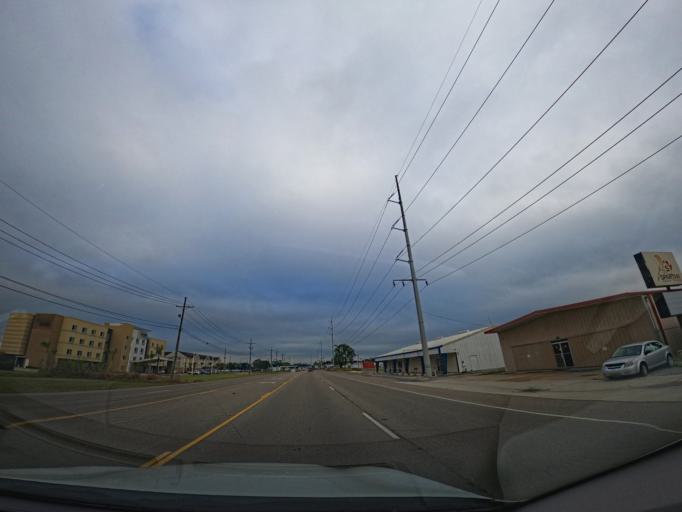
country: US
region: Louisiana
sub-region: Terrebonne Parish
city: Presquille
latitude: 29.5674
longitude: -90.6823
